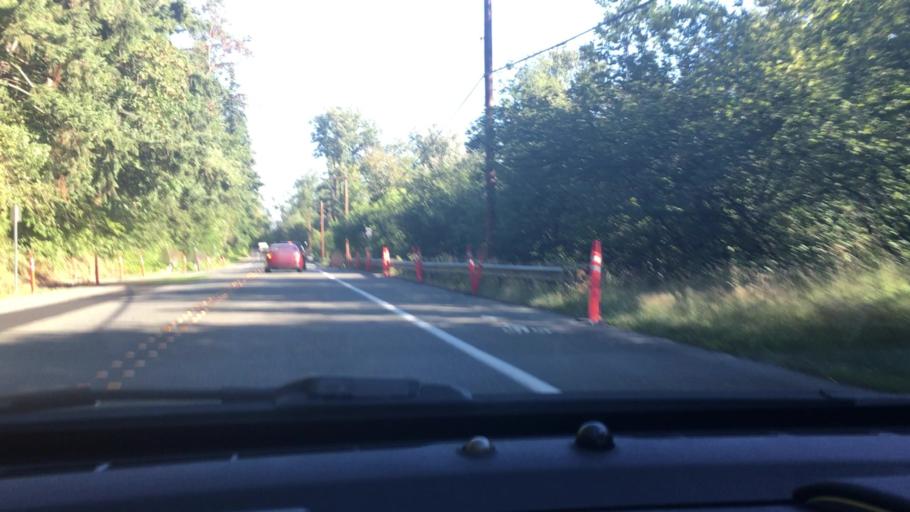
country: US
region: Washington
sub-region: King County
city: Sammamish
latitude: 47.6591
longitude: -122.0952
